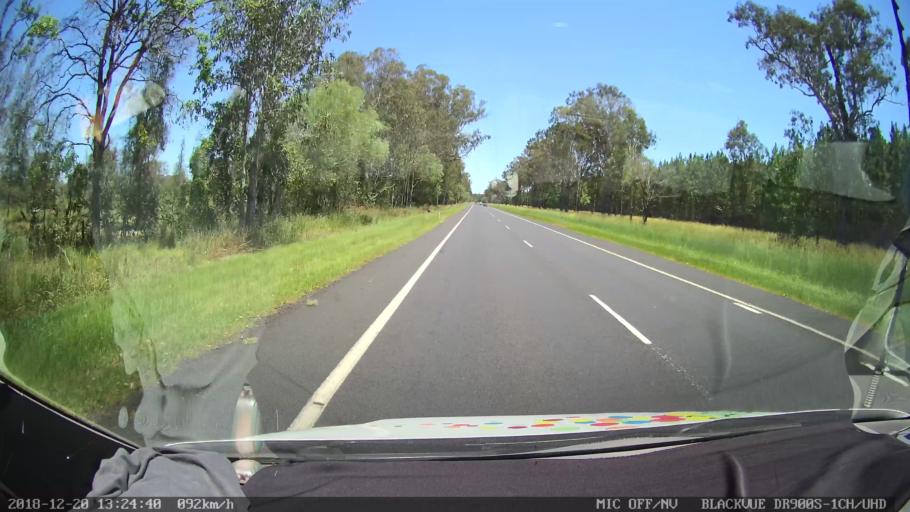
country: AU
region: New South Wales
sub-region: Richmond Valley
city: Casino
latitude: -29.1205
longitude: 152.9994
